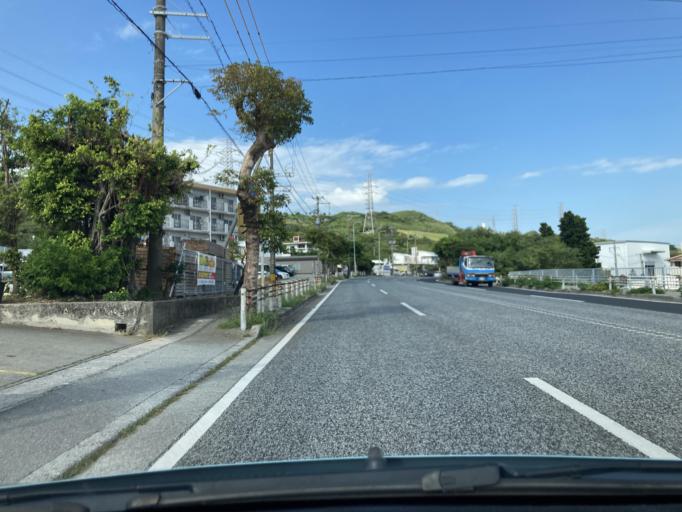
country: JP
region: Okinawa
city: Ginowan
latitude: 26.2698
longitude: 127.7914
